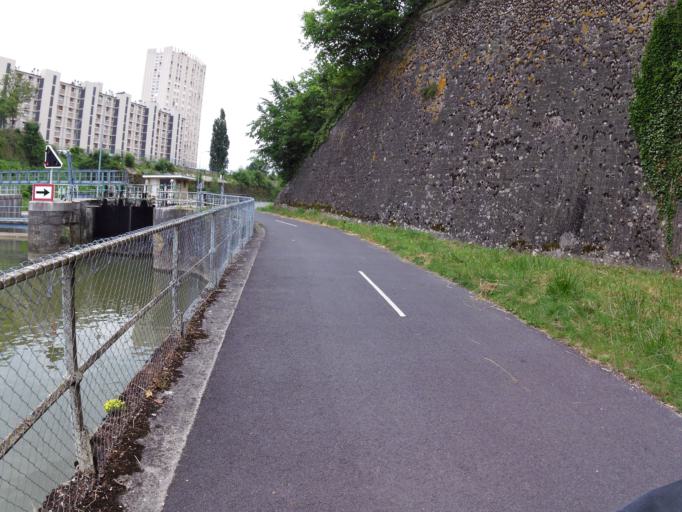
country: FR
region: Champagne-Ardenne
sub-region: Departement des Ardennes
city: Charleville-Mezieres
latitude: 49.7606
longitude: 4.7247
